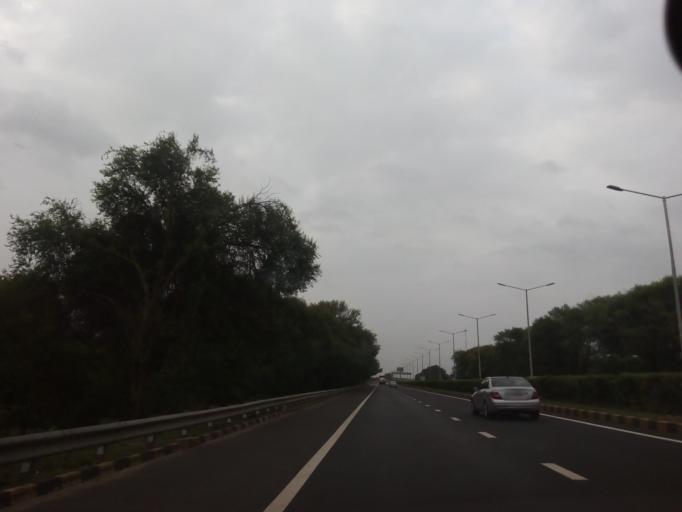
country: IN
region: Gujarat
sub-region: Kheda
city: Nadiad
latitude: 22.6960
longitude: 72.8984
